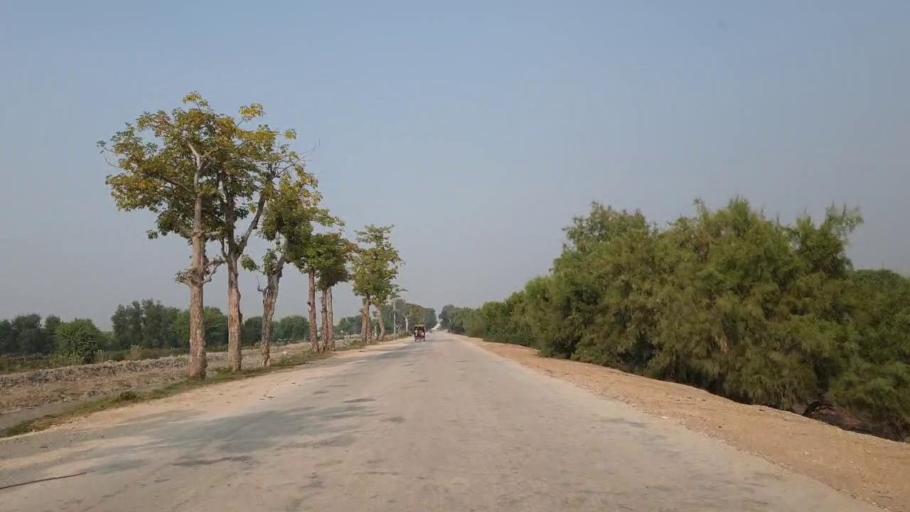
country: PK
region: Sindh
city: Bhan
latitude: 26.5836
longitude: 67.7289
